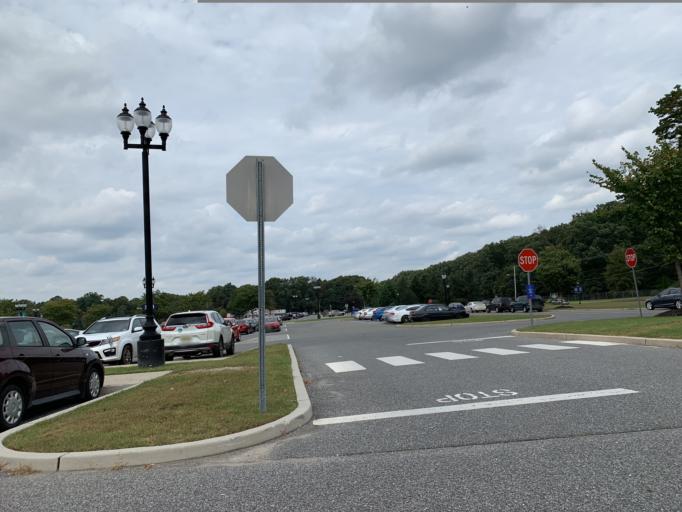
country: US
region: New Jersey
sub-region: Gloucester County
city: Turnersville
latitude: 39.7855
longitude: -75.0361
